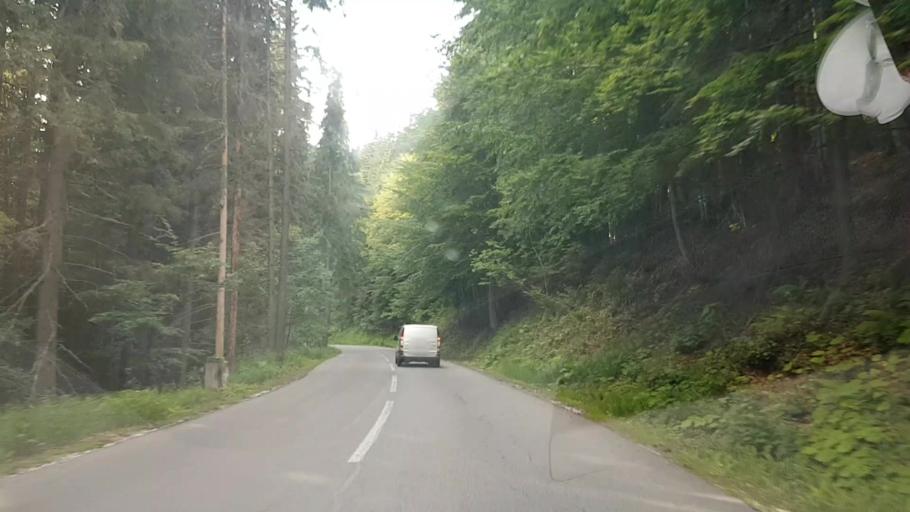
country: RO
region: Harghita
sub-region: Comuna Varsag
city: Varsag
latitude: 46.6718
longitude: 25.3283
